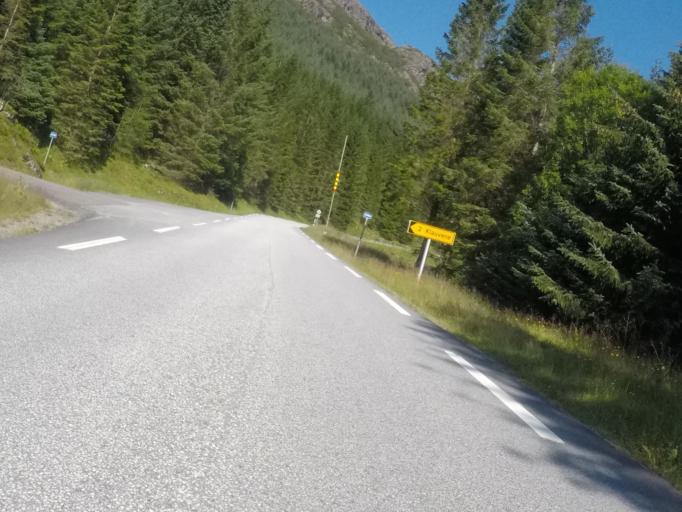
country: NO
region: Sogn og Fjordane
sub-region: Bremanger
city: Svelgen
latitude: 61.6394
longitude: 5.2002
